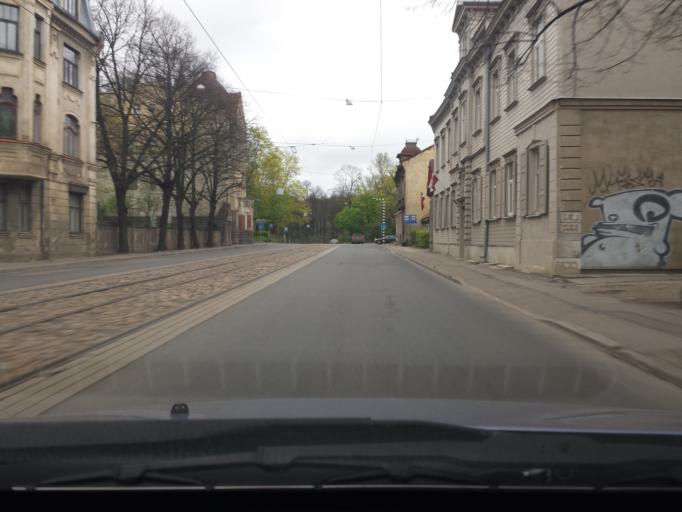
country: LV
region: Riga
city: Riga
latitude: 56.9476
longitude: 24.0729
